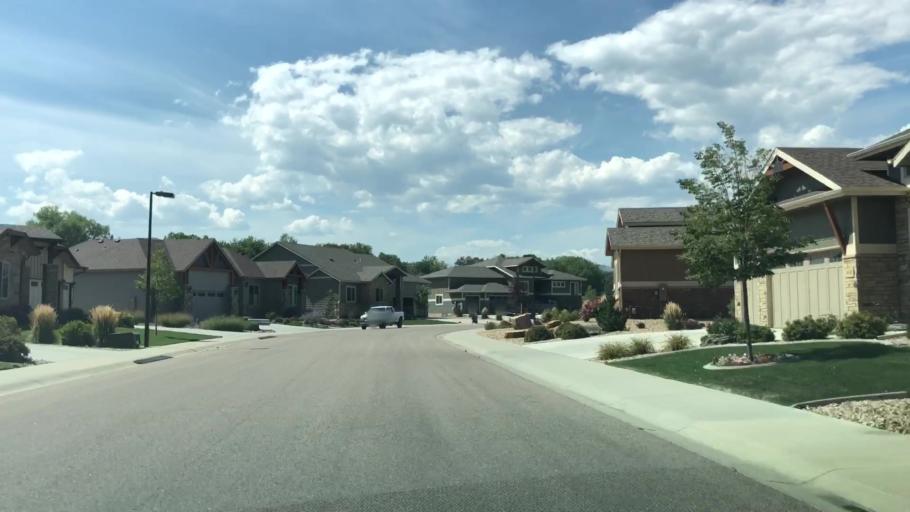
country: US
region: Colorado
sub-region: Larimer County
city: Loveland
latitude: 40.3948
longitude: -105.1566
